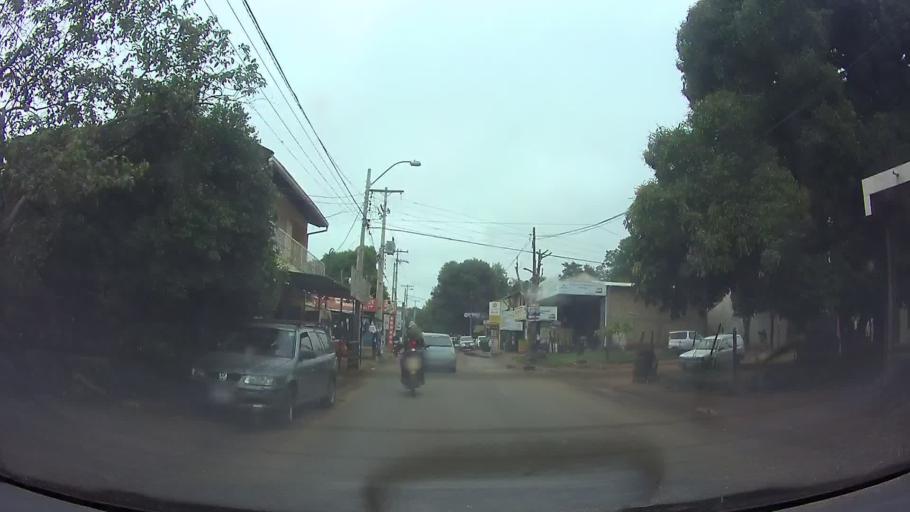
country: PY
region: Central
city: San Lorenzo
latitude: -25.3267
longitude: -57.5031
